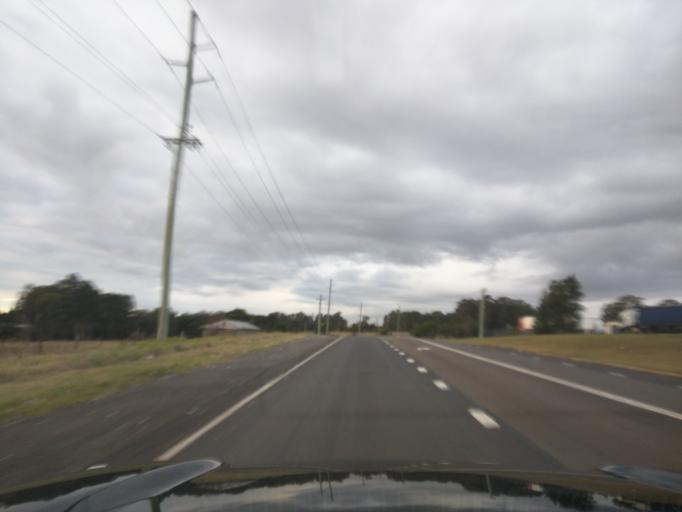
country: AU
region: New South Wales
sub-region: Wollondilly
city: Douglas Park
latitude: -34.2115
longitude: 150.7780
